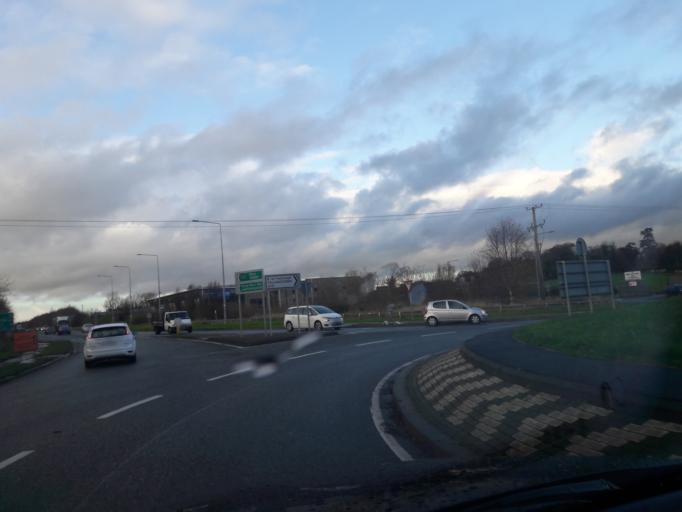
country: IE
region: Leinster
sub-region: Lu
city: Ardee
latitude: 53.8650
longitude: -6.5433
